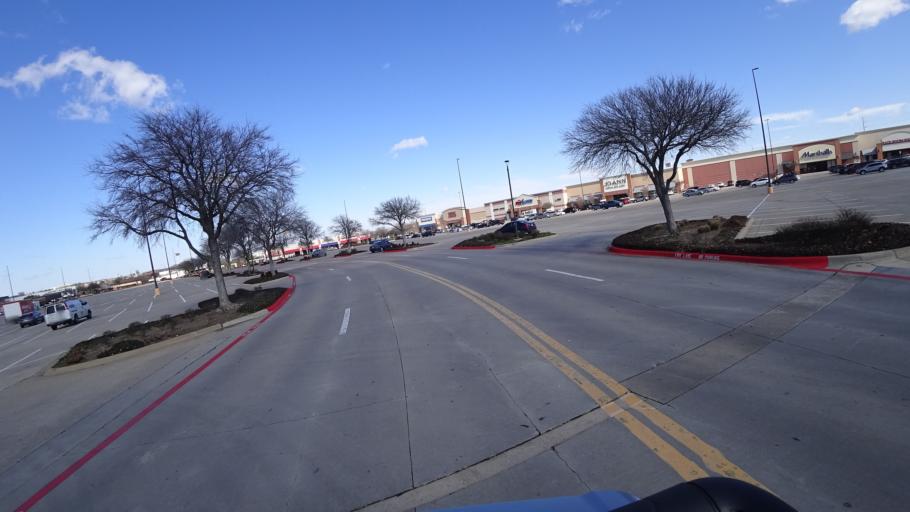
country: US
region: Texas
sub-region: Denton County
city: Lewisville
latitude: 33.0062
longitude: -96.9773
